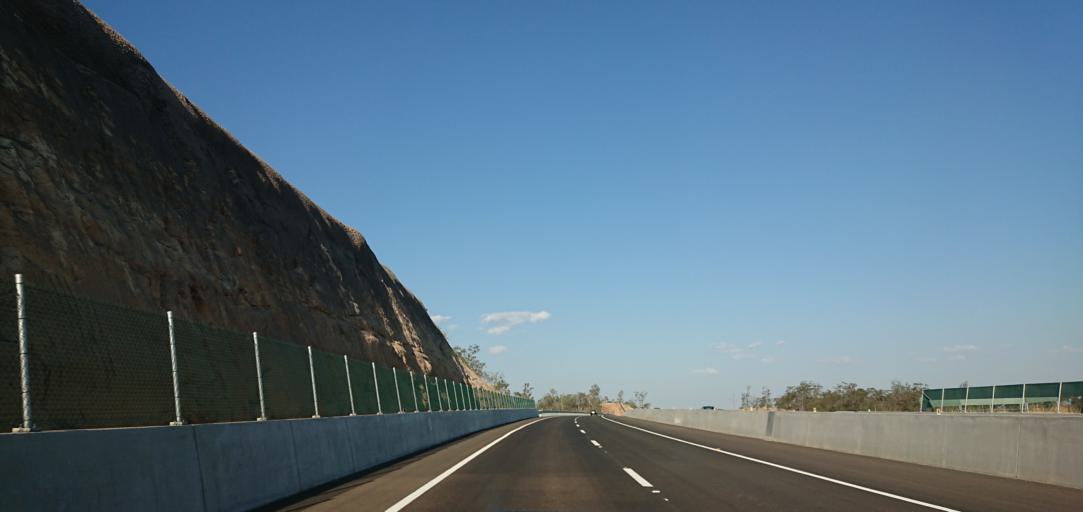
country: AU
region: Queensland
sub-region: Toowoomba
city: East Toowoomba
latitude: -27.5146
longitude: 152.0415
